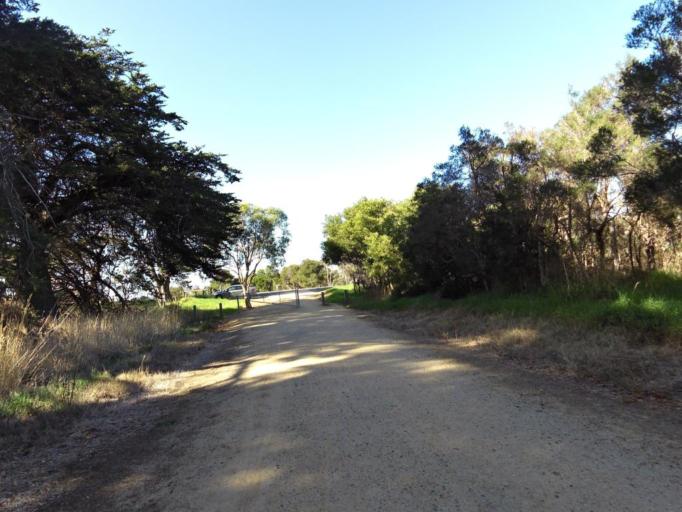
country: AU
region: Victoria
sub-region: Bass Coast
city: North Wonthaggi
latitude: -38.5883
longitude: 145.5576
